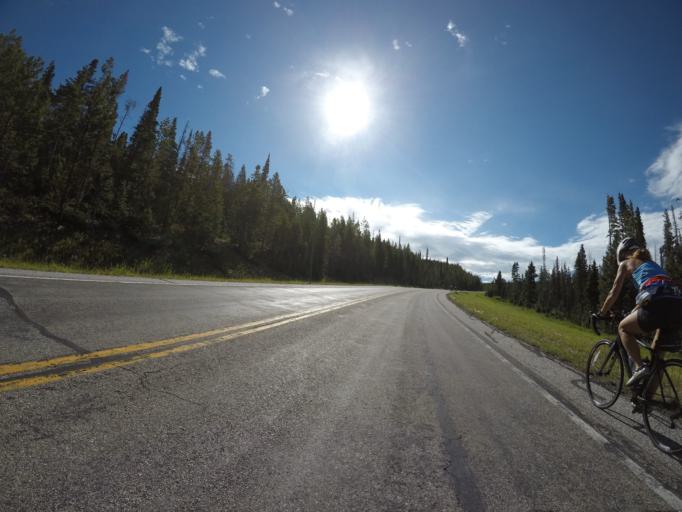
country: US
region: Wyoming
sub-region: Carbon County
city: Saratoga
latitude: 41.3253
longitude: -106.4636
